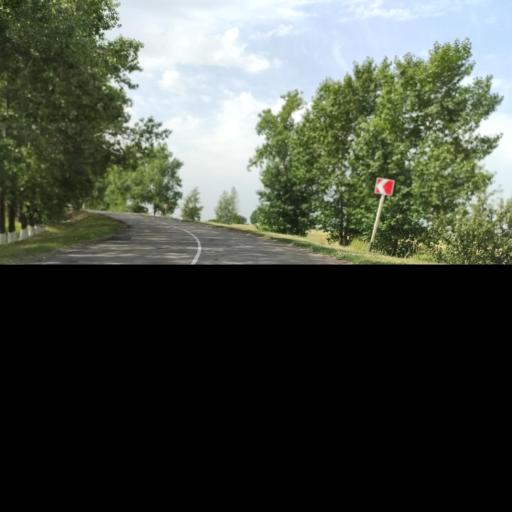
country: RU
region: Voronezj
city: Davydovka
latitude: 51.2474
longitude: 39.5450
